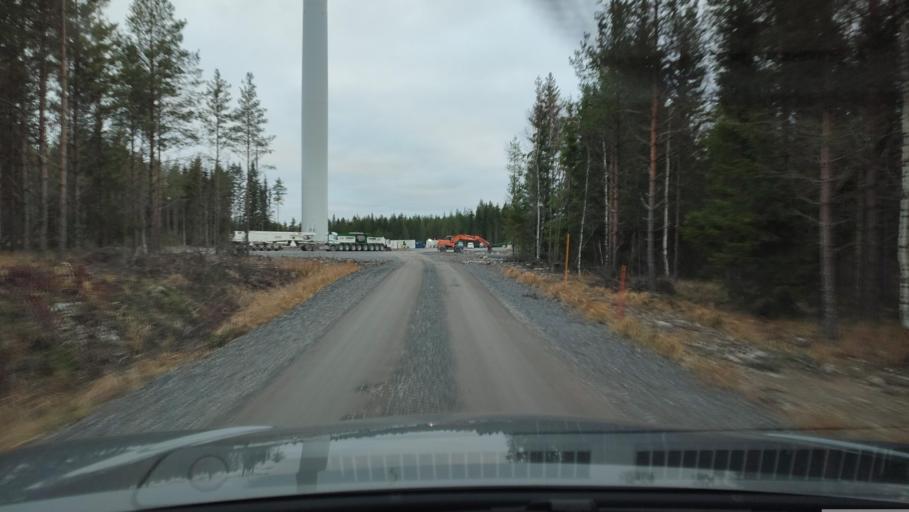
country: FI
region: Southern Ostrobothnia
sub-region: Suupohja
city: Karijoki
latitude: 62.1870
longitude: 21.5632
